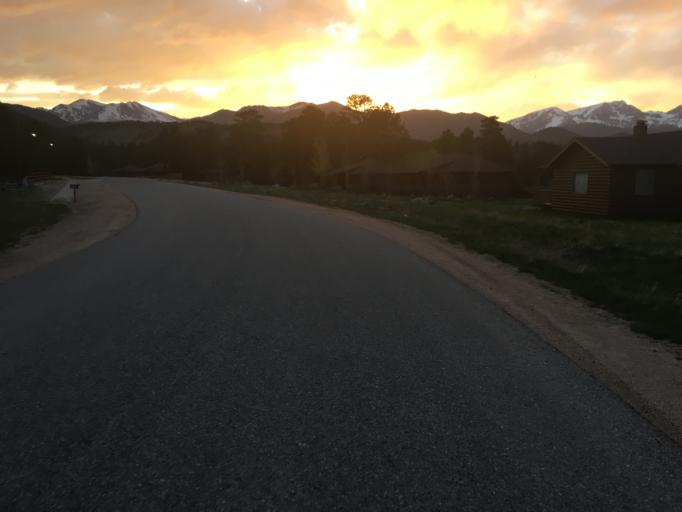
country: US
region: Colorado
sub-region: Larimer County
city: Estes Park
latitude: 40.3425
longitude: -105.5708
